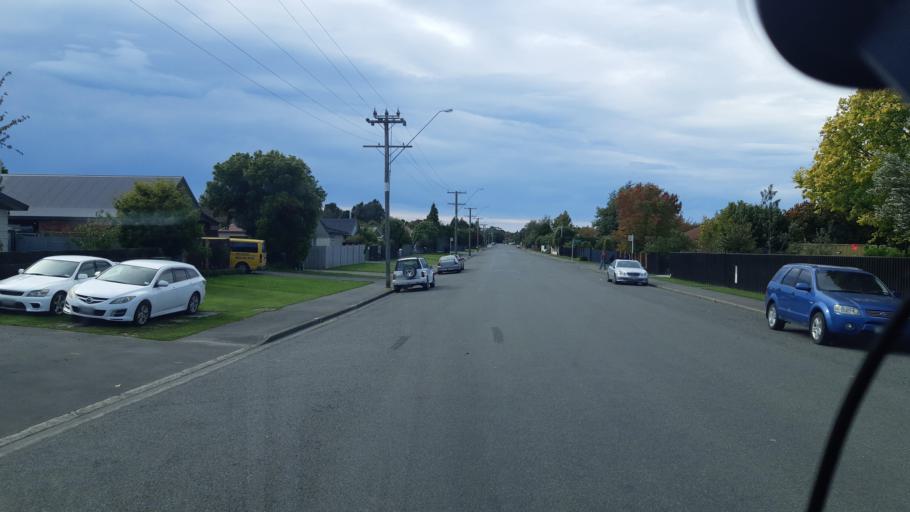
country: NZ
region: Canterbury
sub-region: Waimakariri District
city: Woodend
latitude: -43.3205
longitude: 172.6593
